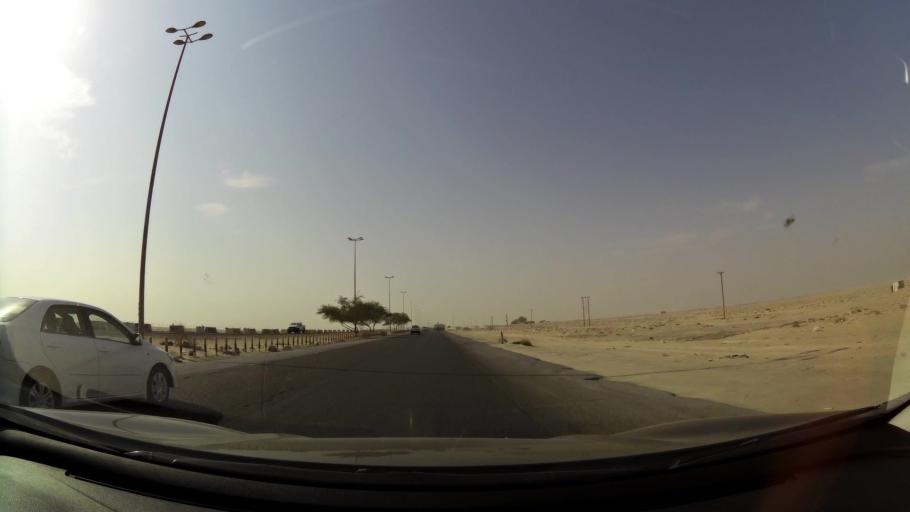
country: KW
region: Al Ahmadi
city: Al Ahmadi
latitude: 28.9176
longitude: 48.0999
